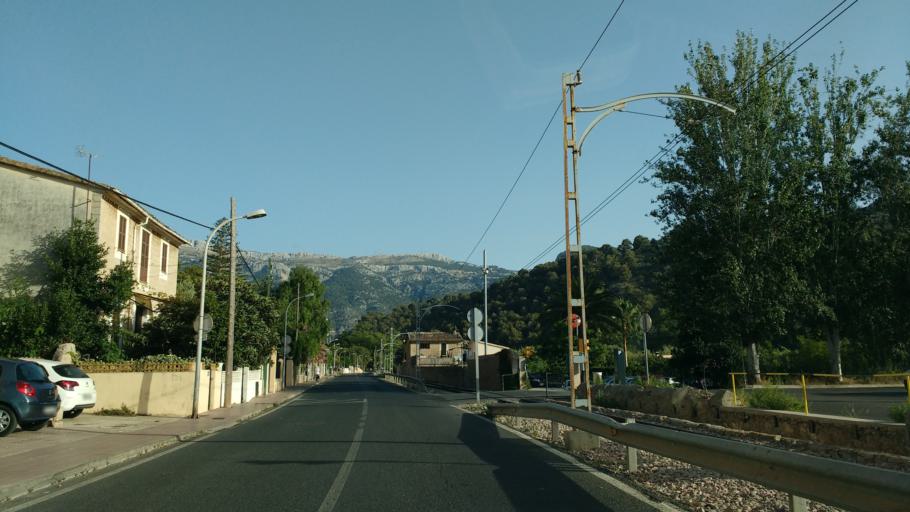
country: ES
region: Balearic Islands
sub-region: Illes Balears
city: Soller
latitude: 39.7898
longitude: 2.6948
